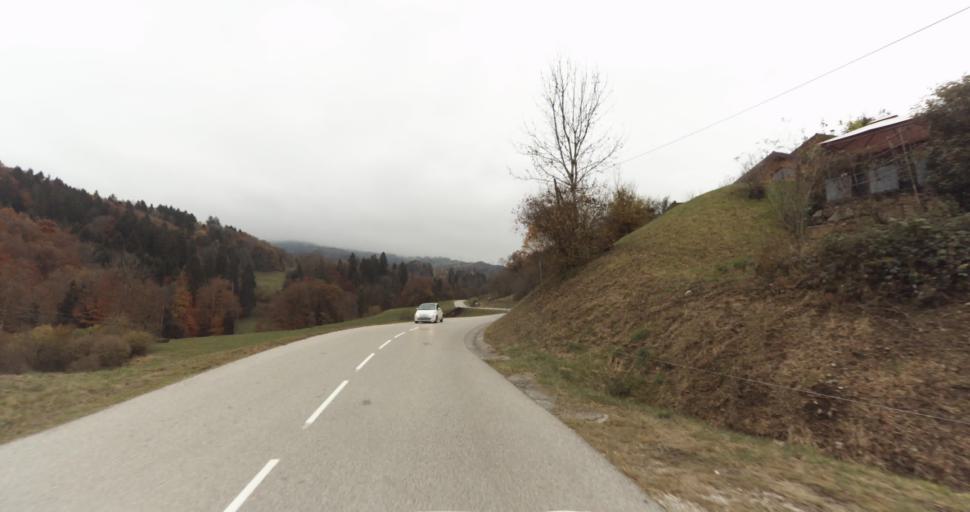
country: FR
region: Rhone-Alpes
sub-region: Departement de la Haute-Savoie
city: Saint-Jorioz
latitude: 45.8103
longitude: 6.1438
